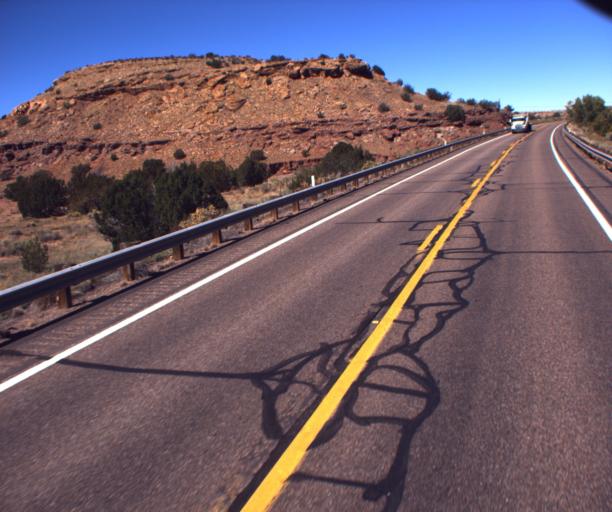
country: US
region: Arizona
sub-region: Apache County
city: Saint Johns
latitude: 34.3766
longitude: -109.4021
